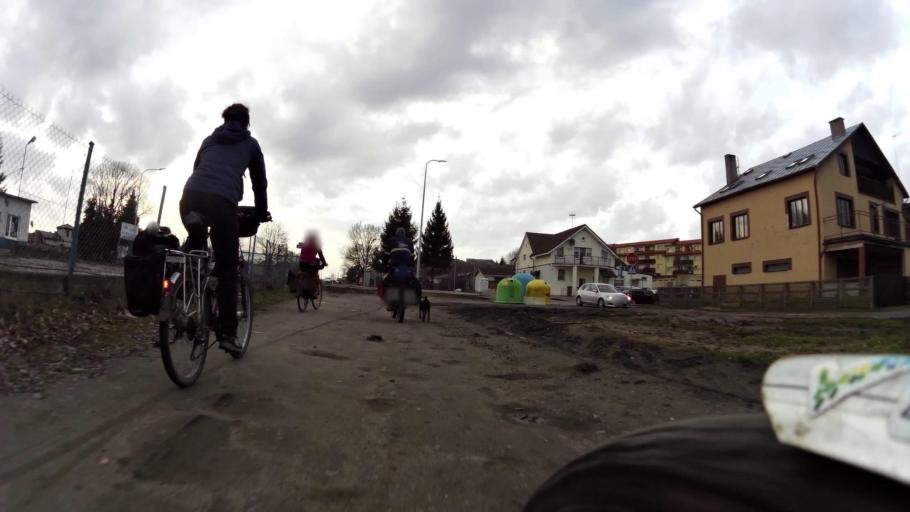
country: PL
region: West Pomeranian Voivodeship
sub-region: Powiat kamienski
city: Kamien Pomorski
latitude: 53.9675
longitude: 14.7655
